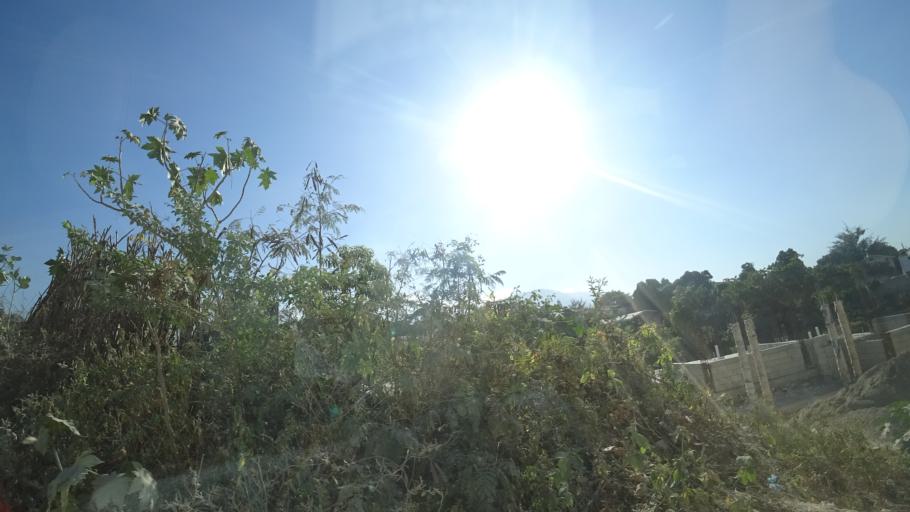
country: HT
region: Ouest
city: Delmas 73
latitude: 18.5384
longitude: -72.2860
